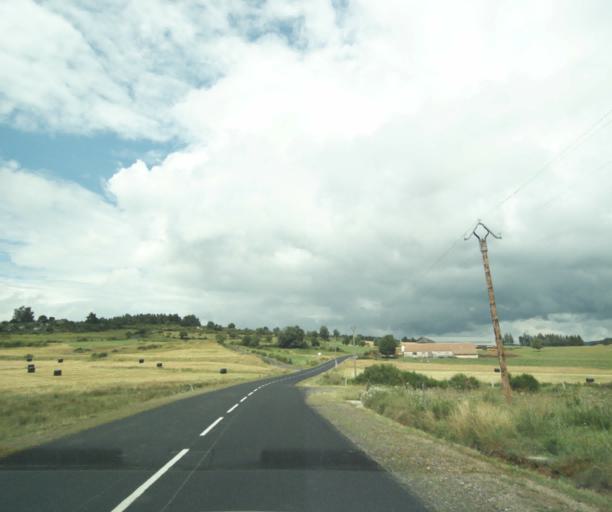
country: FR
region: Auvergne
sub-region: Departement de la Haute-Loire
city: Saugues
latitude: 44.8864
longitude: 3.5042
